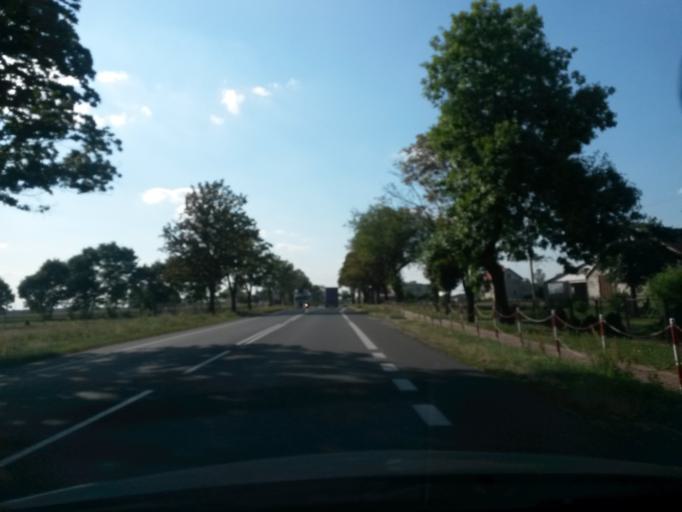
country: PL
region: Masovian Voivodeship
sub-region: Powiat sierpecki
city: Rosciszewo
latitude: 52.8174
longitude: 19.7852
